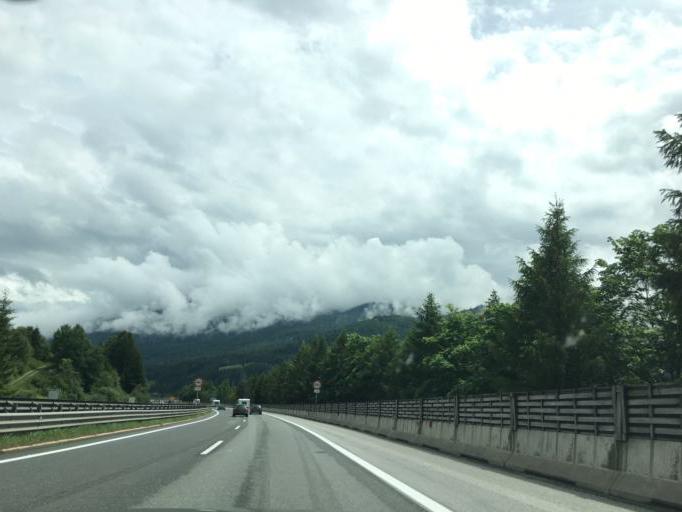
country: AT
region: Salzburg
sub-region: Politischer Bezirk Tamsweg
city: Sankt Michael im Lungau
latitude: 47.1005
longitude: 13.6006
